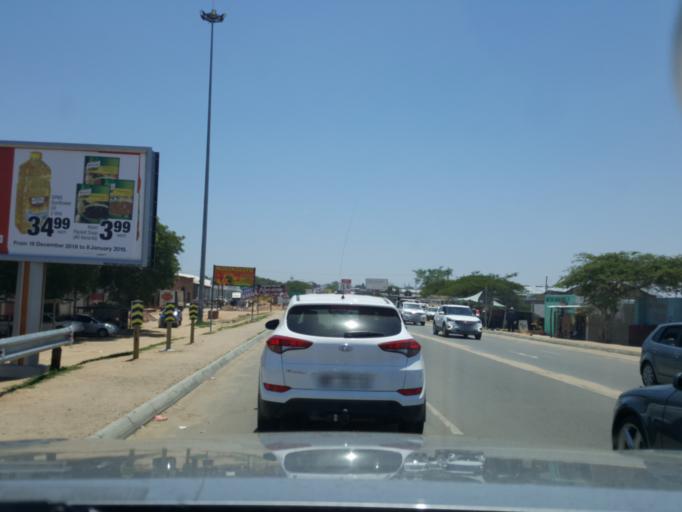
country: ZA
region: Limpopo
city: Thulamahashi
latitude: -24.6028
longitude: 31.0426
